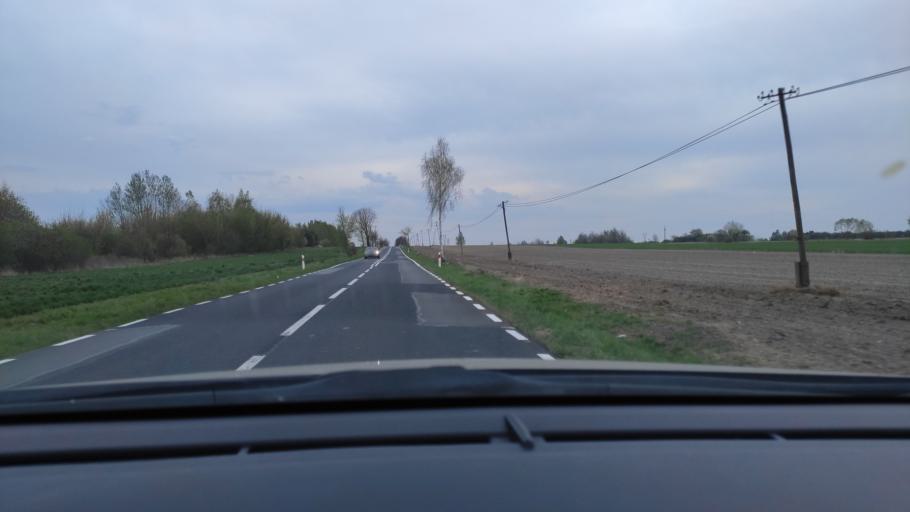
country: PL
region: Masovian Voivodeship
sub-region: Powiat zwolenski
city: Zwolen
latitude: 51.3745
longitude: 21.5631
